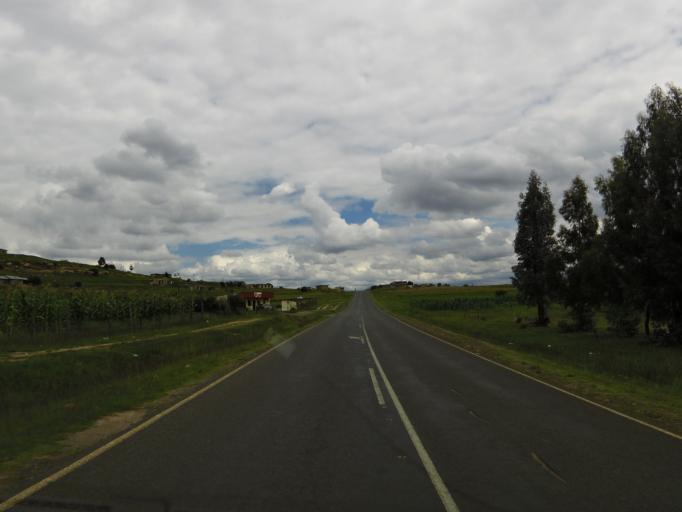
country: LS
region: Leribe
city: Leribe
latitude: -28.9451
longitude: 28.1699
